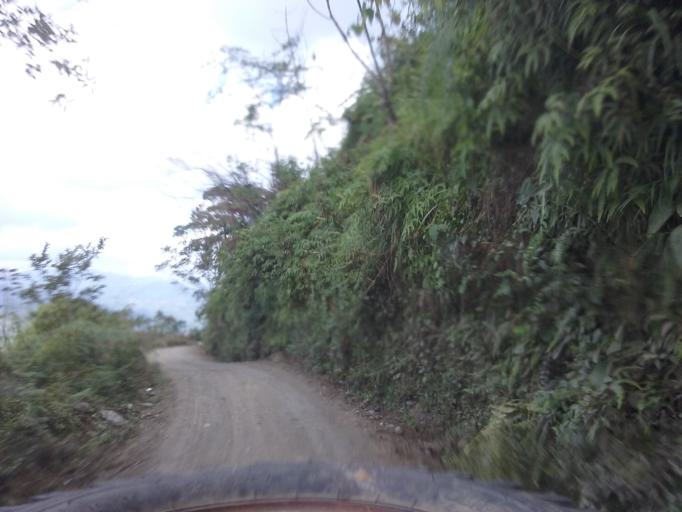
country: CO
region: Tolima
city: Libano
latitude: 4.8043
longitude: -75.0463
